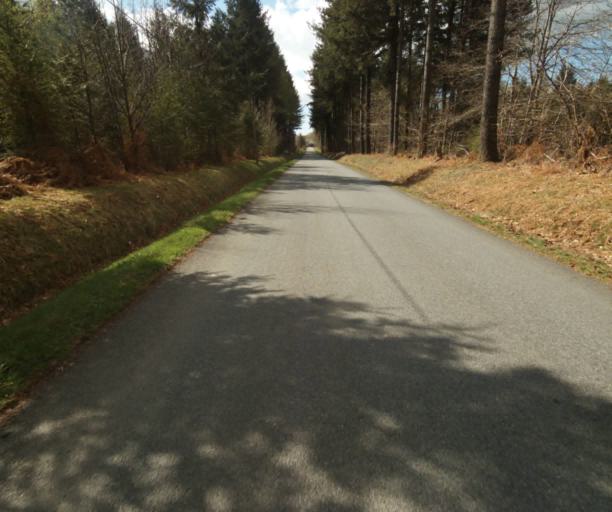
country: FR
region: Limousin
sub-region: Departement de la Correze
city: Argentat
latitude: 45.2305
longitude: 1.9348
